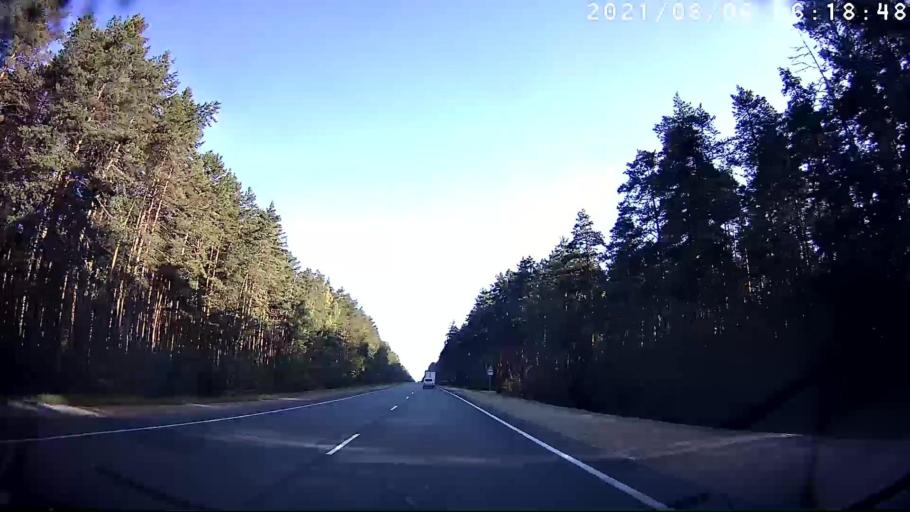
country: RU
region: Mariy-El
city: Pomary
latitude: 56.0314
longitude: 48.3819
